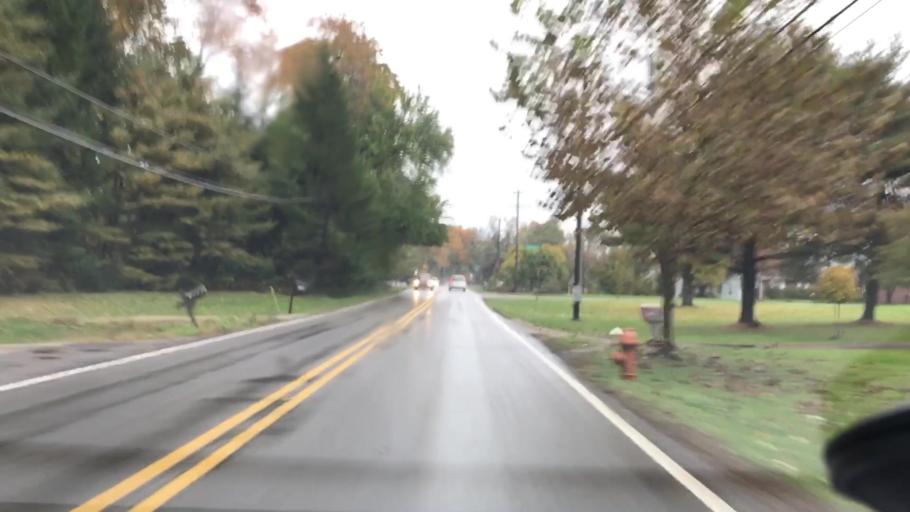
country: US
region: Ohio
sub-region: Franklin County
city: Minerva Park
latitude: 40.0410
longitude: -82.9300
